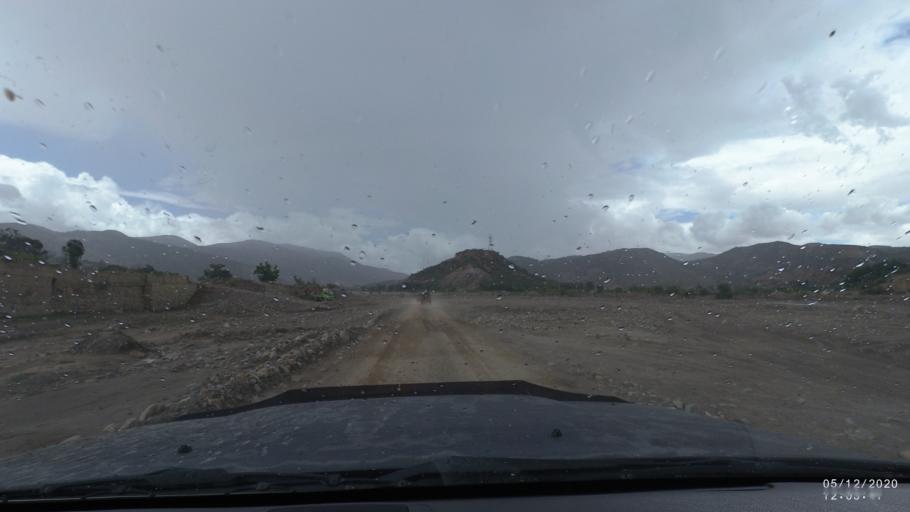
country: BO
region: Cochabamba
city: Sipe Sipe
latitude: -17.5718
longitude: -66.3532
